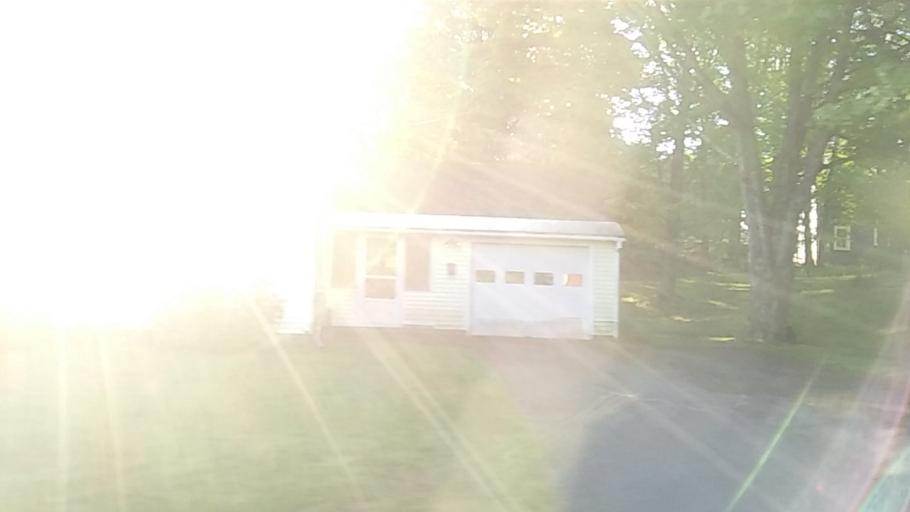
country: US
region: Massachusetts
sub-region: Franklin County
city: Shelburne Falls
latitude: 42.5963
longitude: -72.7400
